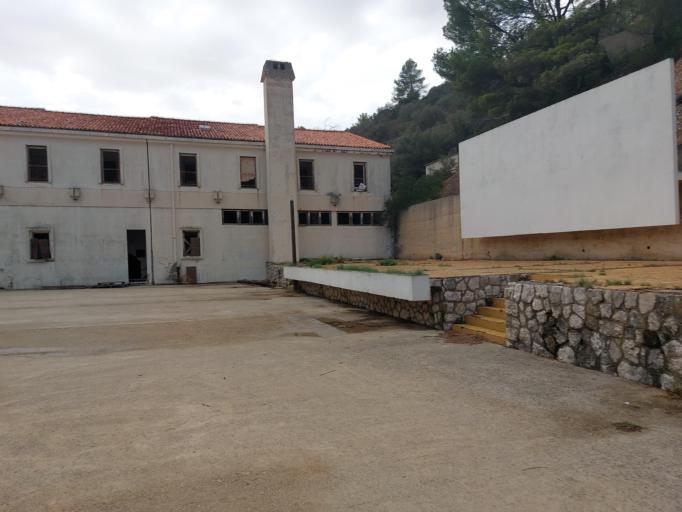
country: HR
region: Dubrovacko-Neretvanska
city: Smokvica
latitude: 42.7439
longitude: 16.8275
